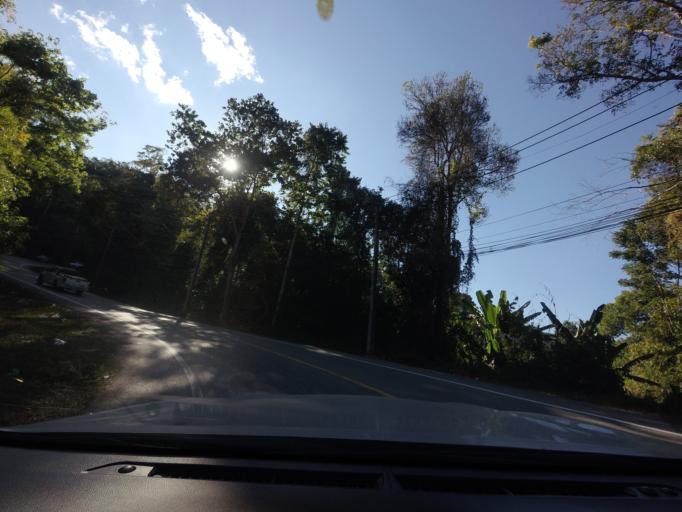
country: TH
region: Chiang Mai
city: Mae Taeng
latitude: 19.1260
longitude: 98.7438
